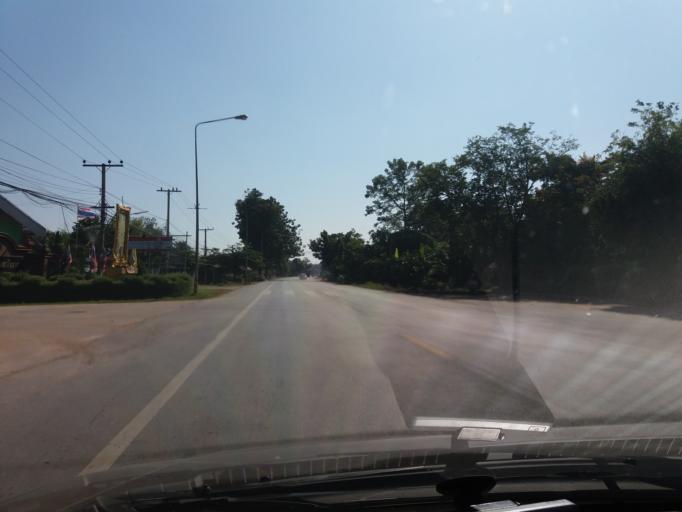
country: TH
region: Kamphaeng Phet
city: Khlong Khlung
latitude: 16.2061
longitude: 99.7594
